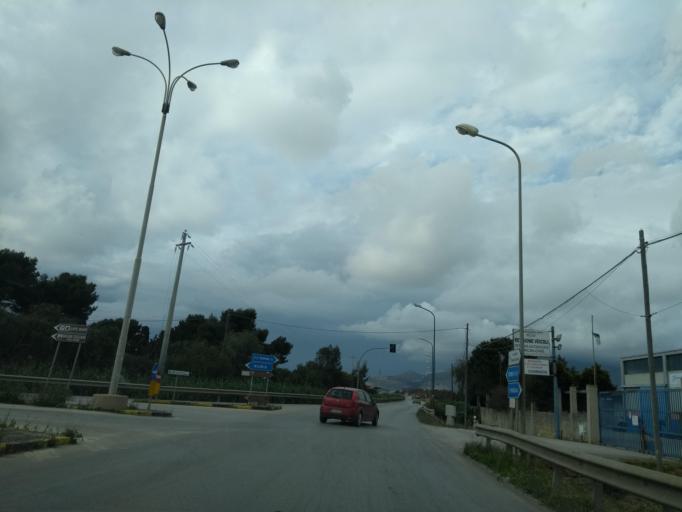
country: IT
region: Sicily
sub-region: Trapani
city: Paceco
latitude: 37.9838
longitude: 12.5317
